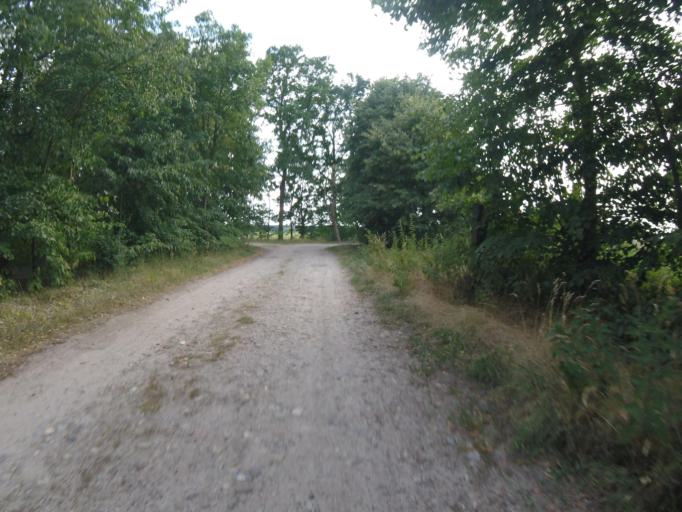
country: DE
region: Brandenburg
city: Spreenhagen
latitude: 52.2957
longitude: 13.8010
